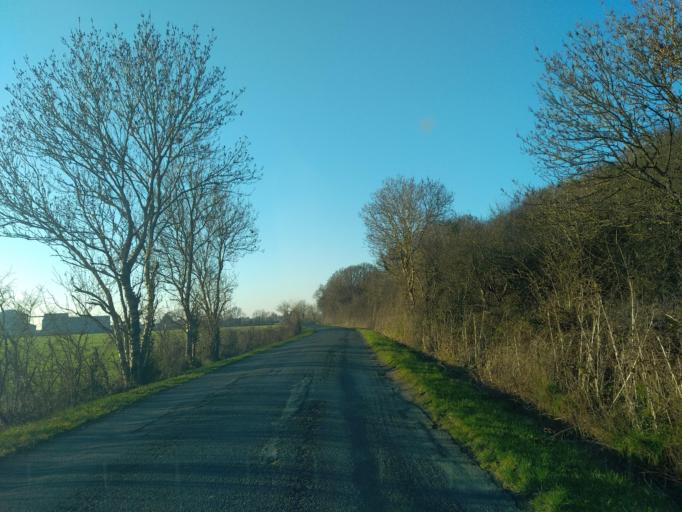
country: FR
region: Pays de la Loire
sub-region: Departement de la Vendee
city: Triaize
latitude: 46.3937
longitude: -1.2941
